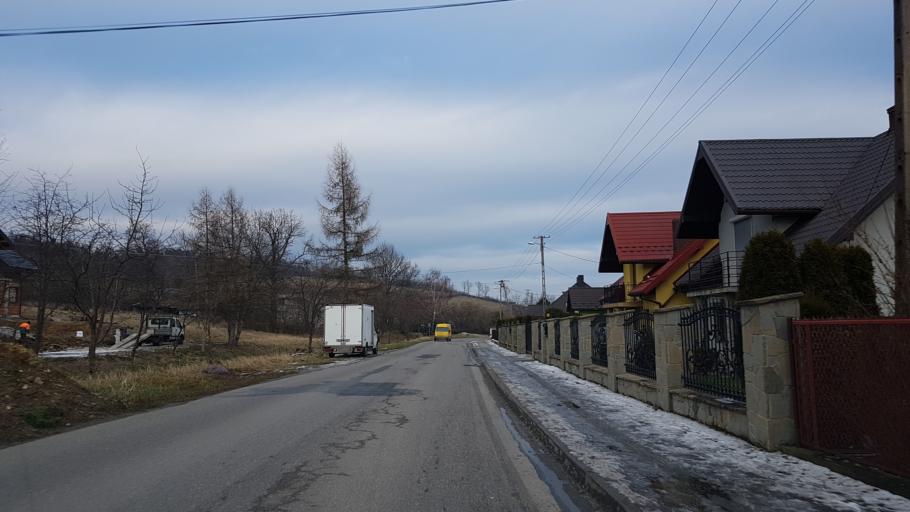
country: PL
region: Lesser Poland Voivodeship
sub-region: Powiat nowosadecki
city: Stary Sacz
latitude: 49.5453
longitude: 20.6174
